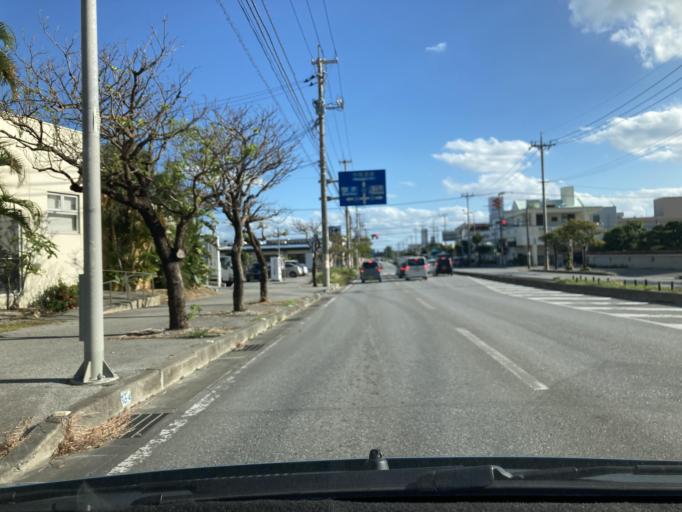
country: JP
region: Okinawa
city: Gushikawa
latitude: 26.3412
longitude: 127.8440
